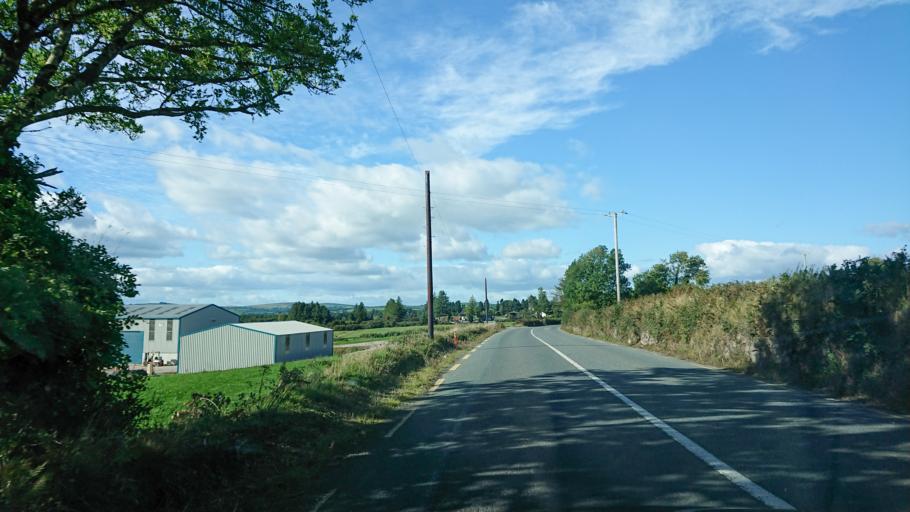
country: IE
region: Munster
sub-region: Waterford
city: Dungarvan
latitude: 52.1890
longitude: -7.6967
